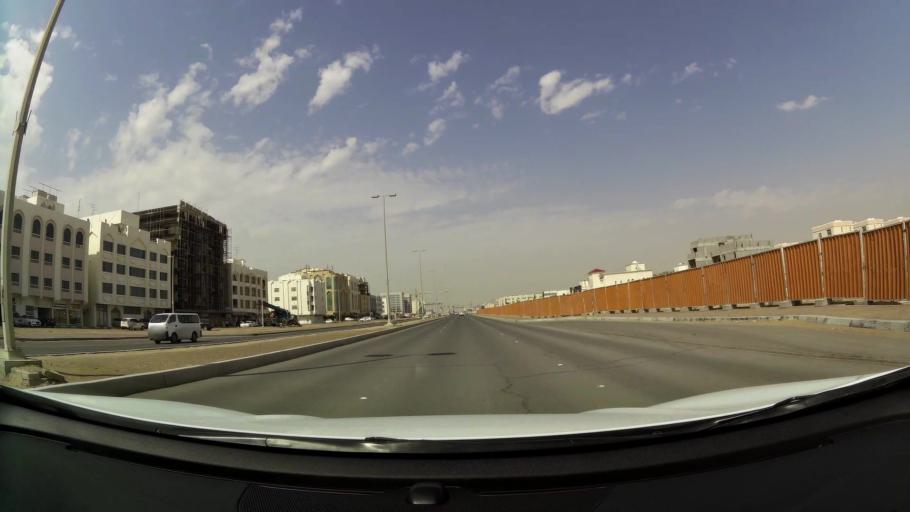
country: AE
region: Abu Dhabi
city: Abu Dhabi
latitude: 24.3348
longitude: 54.5387
